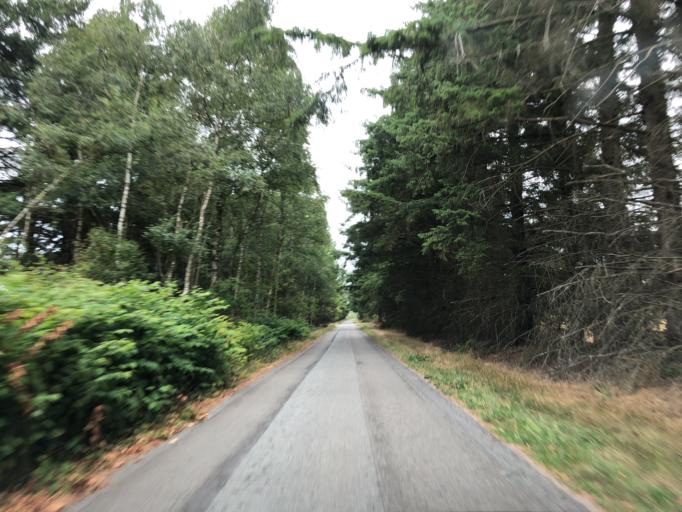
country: DK
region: Central Jutland
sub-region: Holstebro Kommune
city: Ulfborg
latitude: 56.2172
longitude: 8.3201
